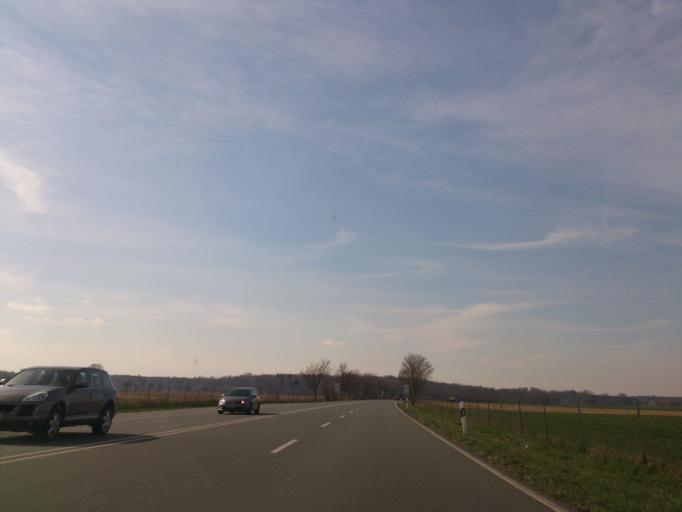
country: DE
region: North Rhine-Westphalia
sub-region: Regierungsbezirk Detmold
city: Salzkotten
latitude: 51.6420
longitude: 8.6538
